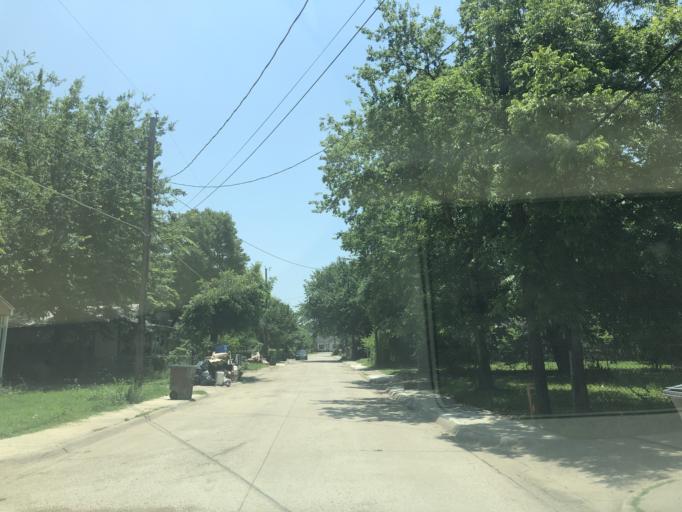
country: US
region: Texas
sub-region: Dallas County
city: Dallas
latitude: 32.7850
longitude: -96.8430
